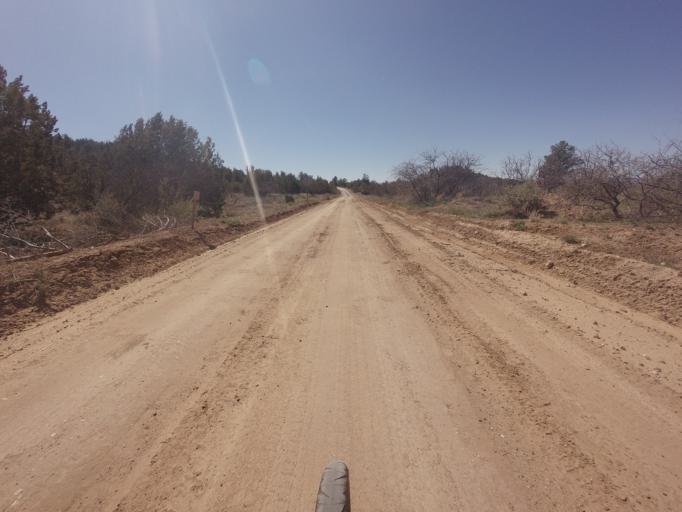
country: US
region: Arizona
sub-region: Yavapai County
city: Lake Montezuma
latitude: 34.5924
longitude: -111.7311
